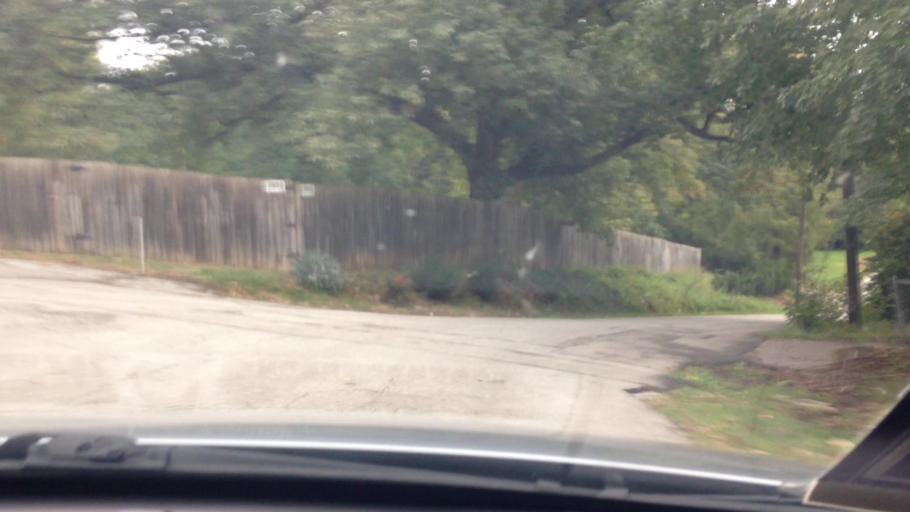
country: US
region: Missouri
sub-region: Clay County
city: North Kansas City
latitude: 39.1622
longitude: -94.5493
